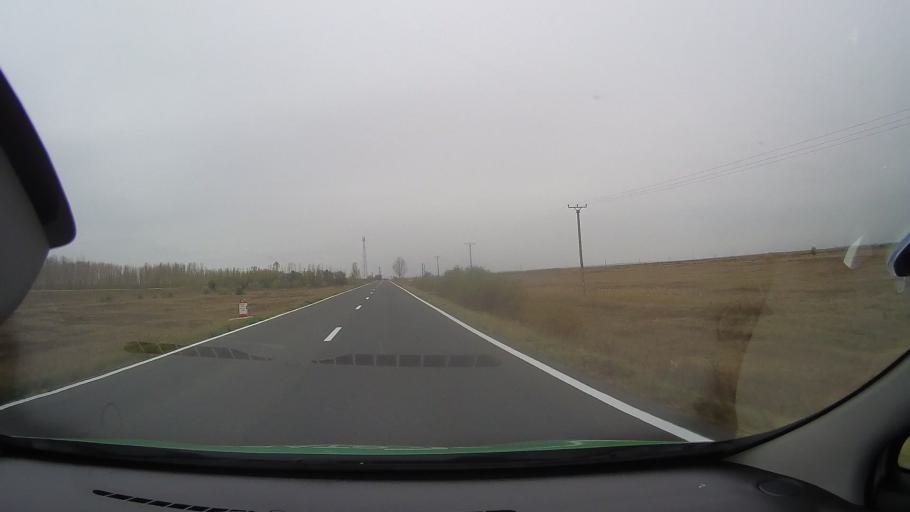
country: RO
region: Ialomita
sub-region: Comuna Giurgeni
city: Giurgeni
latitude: 44.7271
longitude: 27.8538
